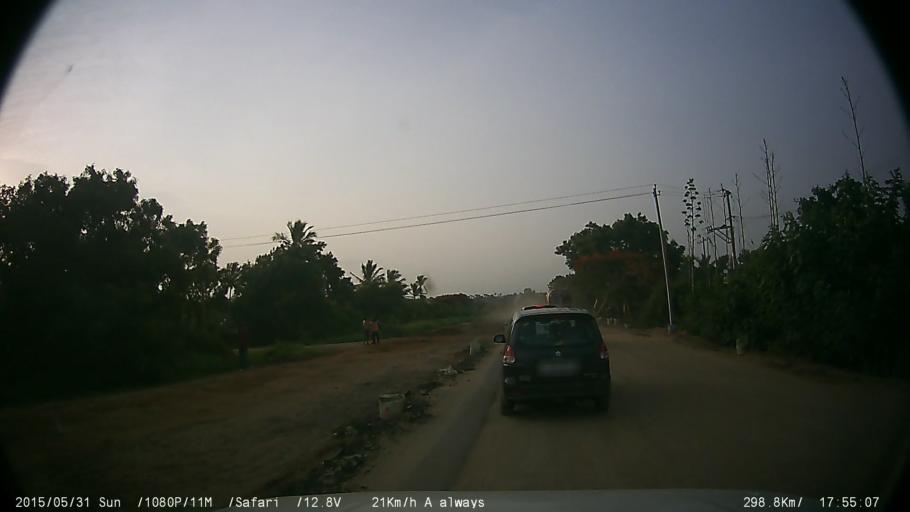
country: IN
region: Karnataka
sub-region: Mysore
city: Nanjangud
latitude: 11.9898
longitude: 76.6700
